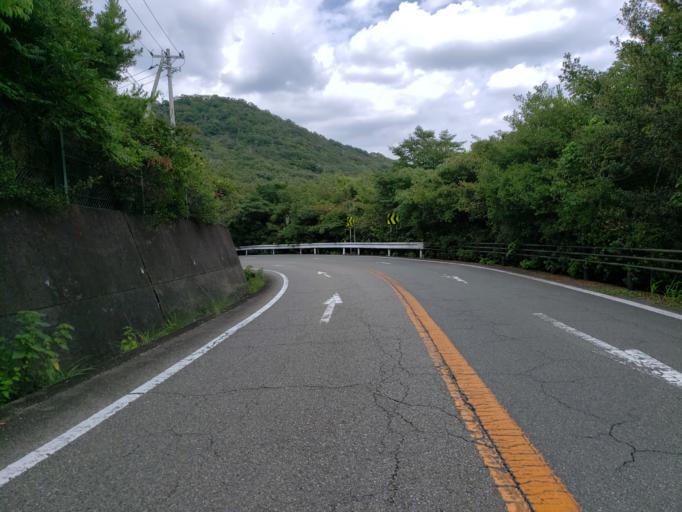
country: JP
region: Hyogo
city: Aioi
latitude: 34.7673
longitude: 134.4794
